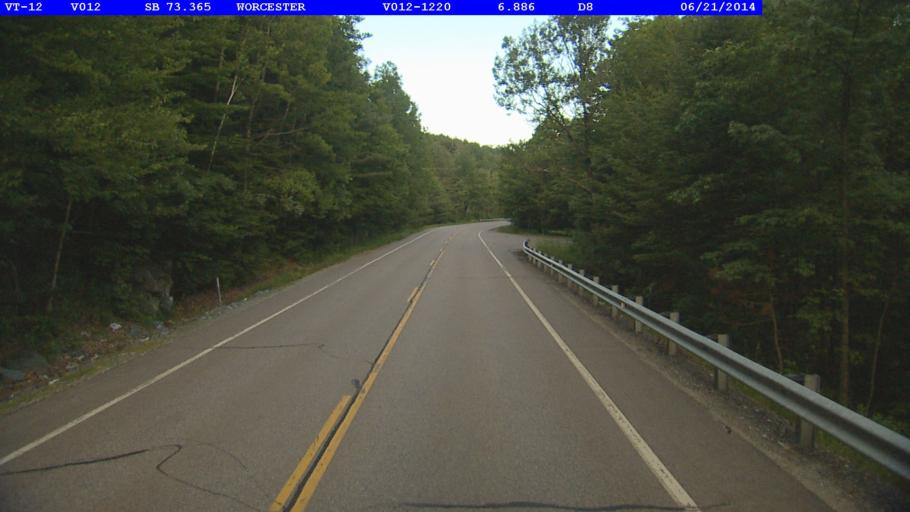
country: US
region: Vermont
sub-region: Lamoille County
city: Morrisville
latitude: 44.4399
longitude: -72.5382
